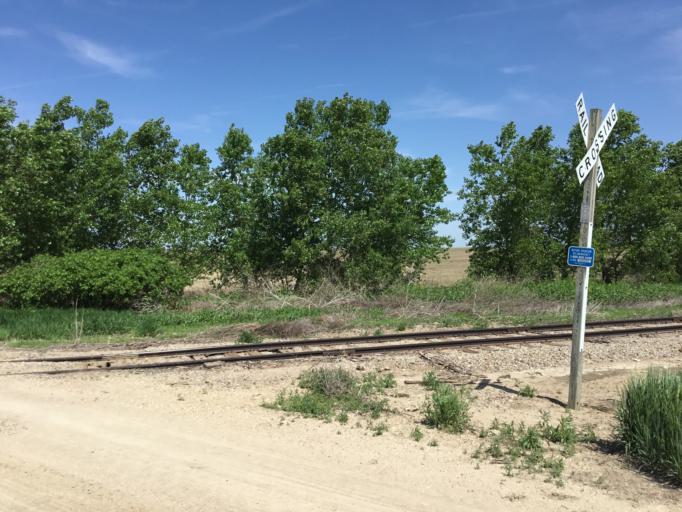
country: US
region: Kansas
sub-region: Mitchell County
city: Beloit
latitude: 39.5100
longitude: -98.0197
